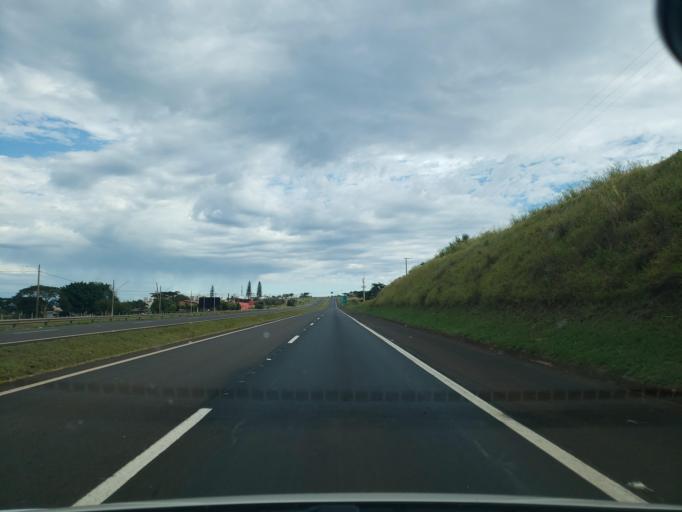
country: BR
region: Sao Paulo
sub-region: Jau
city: Jau
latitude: -22.2603
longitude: -48.5382
